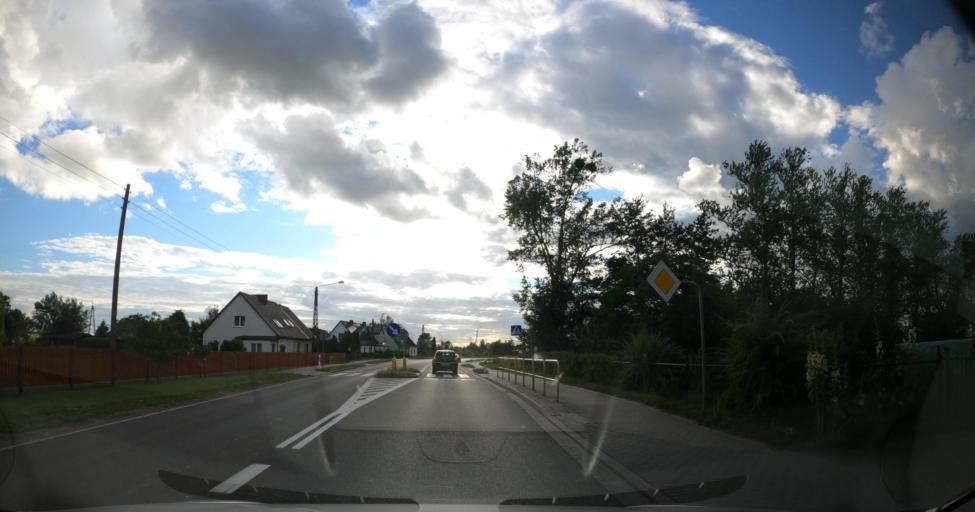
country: PL
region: Pomeranian Voivodeship
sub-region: Powiat slupski
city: Potegowo
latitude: 54.4204
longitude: 17.3842
